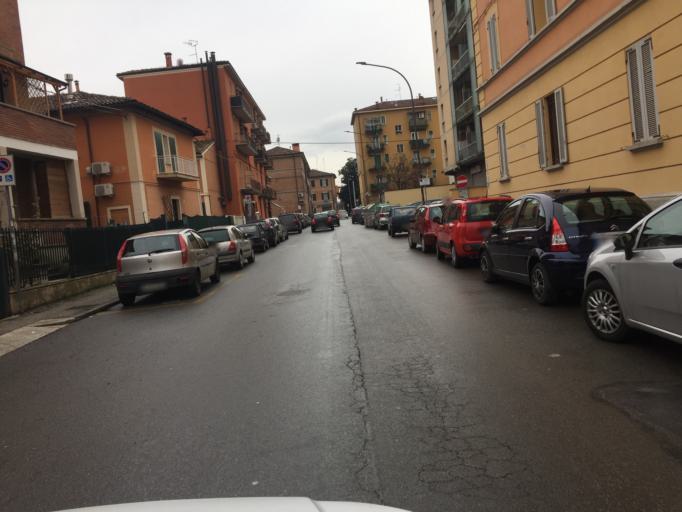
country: IT
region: Emilia-Romagna
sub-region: Provincia di Bologna
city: Casalecchio di Reno
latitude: 44.5100
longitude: 11.2977
